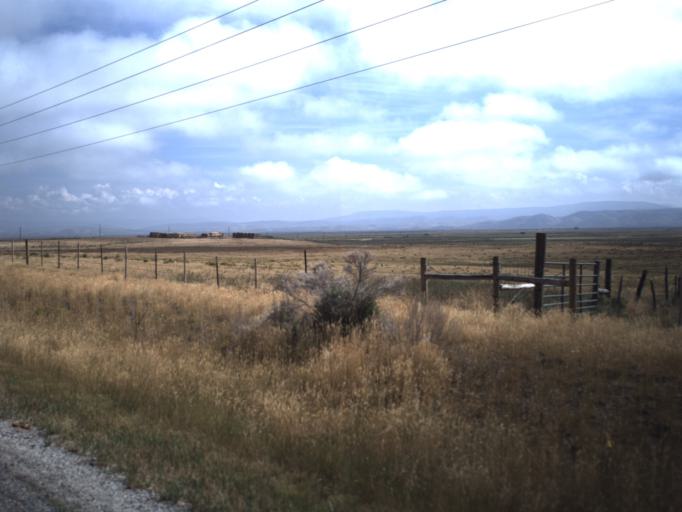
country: US
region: Utah
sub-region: Rich County
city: Randolph
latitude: 41.7450
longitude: -111.1501
